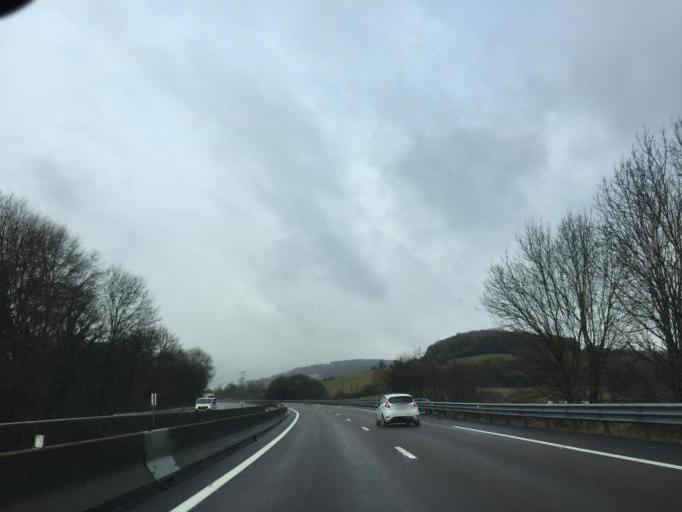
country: FR
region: Bourgogne
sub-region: Departement de la Cote-d'Or
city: Pouilly-en-Auxois
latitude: 47.1842
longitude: 4.6785
